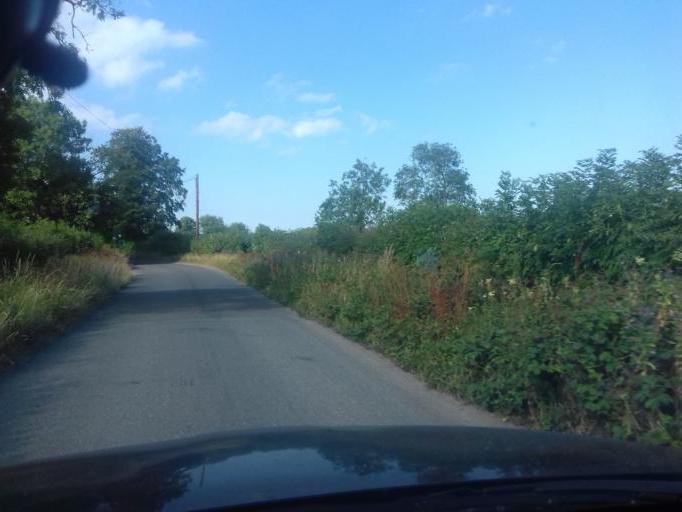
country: IE
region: Leinster
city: Hartstown
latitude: 53.4304
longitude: -6.4279
